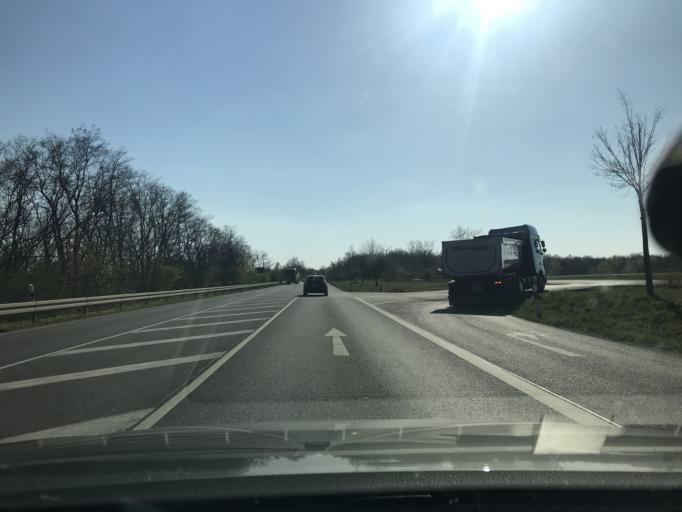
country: DE
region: Saxony-Anhalt
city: Zscherndorf
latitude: 51.5961
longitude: 12.2765
